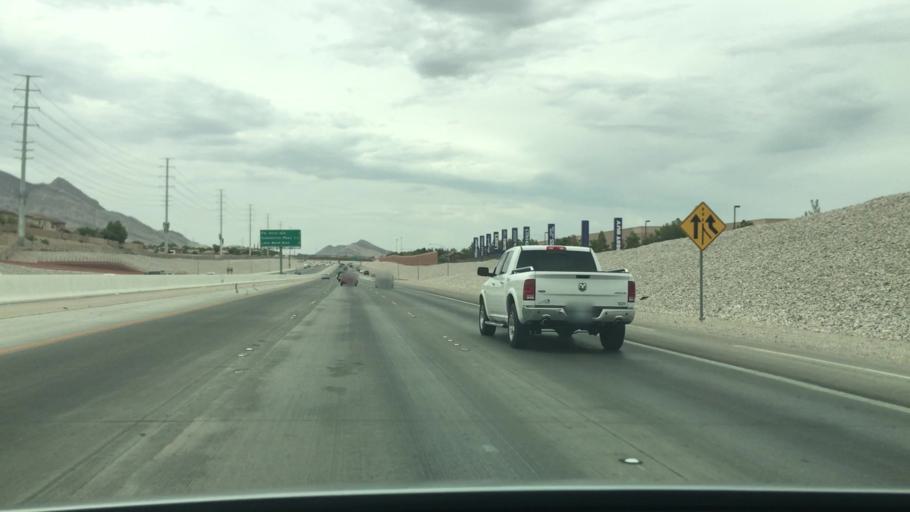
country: US
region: Nevada
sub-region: Clark County
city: Summerlin South
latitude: 36.1605
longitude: -115.3372
